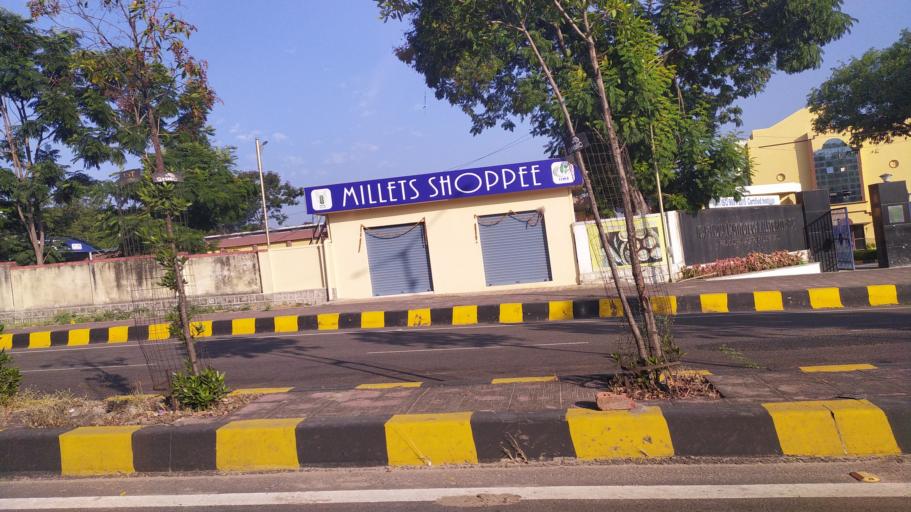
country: IN
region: Telangana
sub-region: Hyderabad
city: Hyderabad
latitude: 17.3203
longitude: 78.3962
